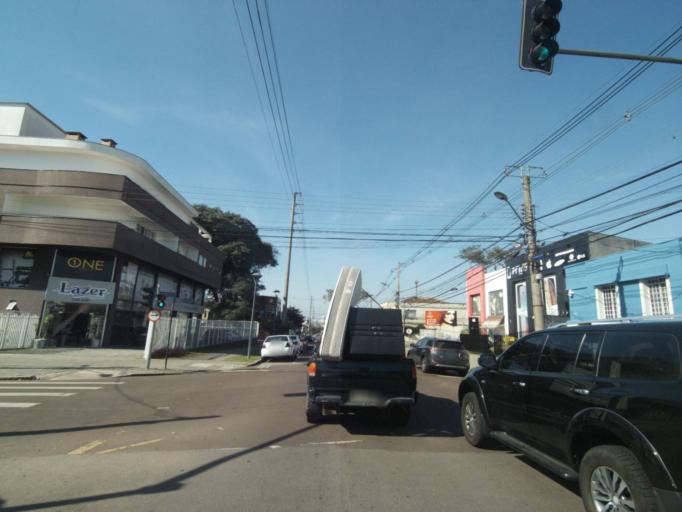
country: BR
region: Parana
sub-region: Curitiba
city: Curitiba
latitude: -25.4493
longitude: -49.2749
